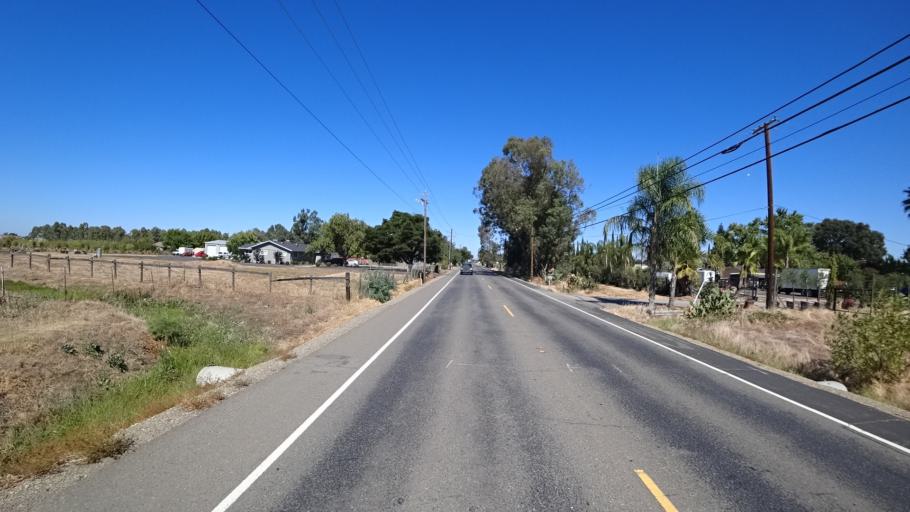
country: US
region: California
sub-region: Sacramento County
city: Vineyard
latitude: 38.4308
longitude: -121.3347
